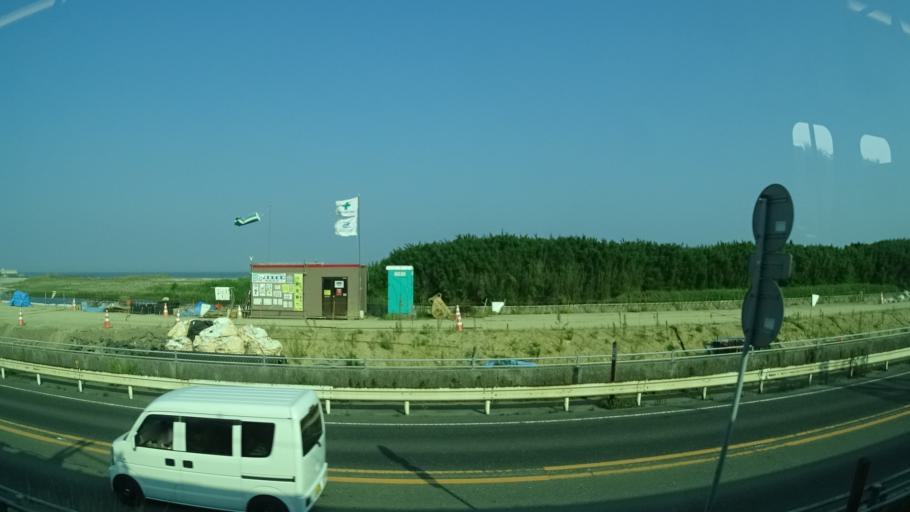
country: JP
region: Ibaraki
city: Kitaibaraki
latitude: 36.7937
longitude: 140.7519
